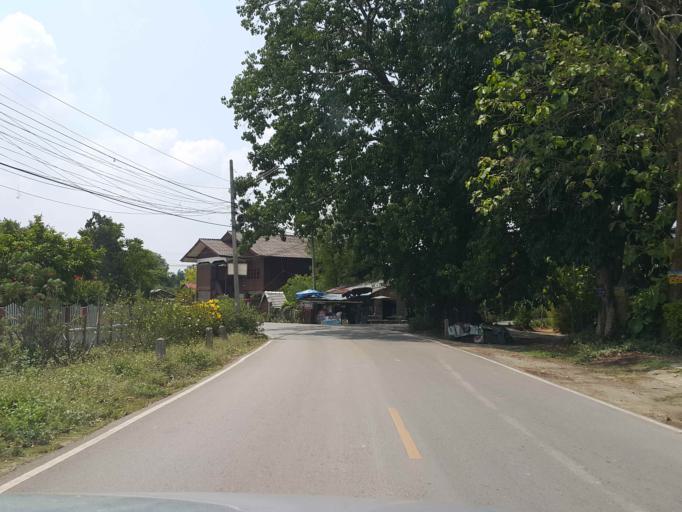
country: TH
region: Chiang Mai
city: Saraphi
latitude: 18.6837
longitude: 98.9989
